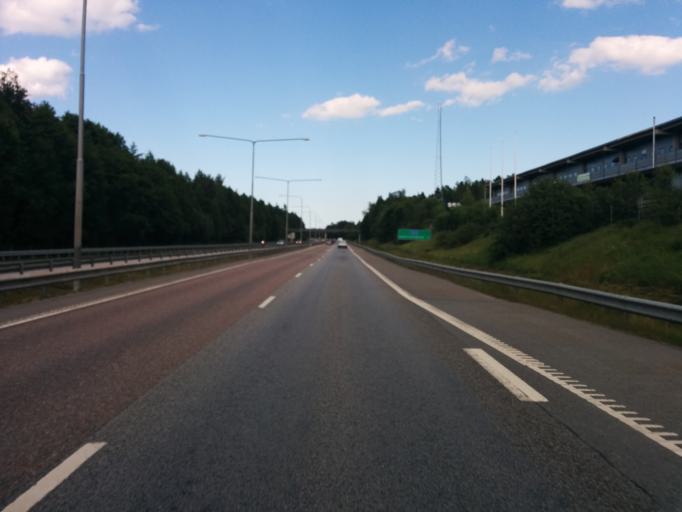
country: SE
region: Stockholm
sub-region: Nacka Kommun
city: Boo
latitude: 59.3162
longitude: 18.2661
